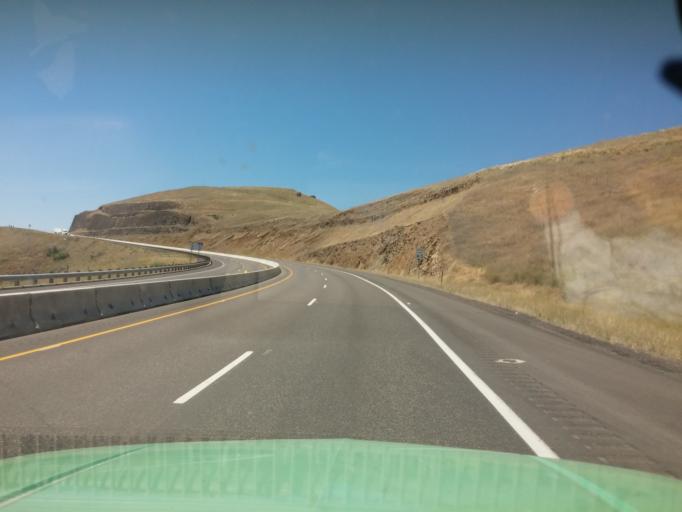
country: US
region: Idaho
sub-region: Nez Perce County
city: Lewiston
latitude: 46.4628
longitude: -116.9830
